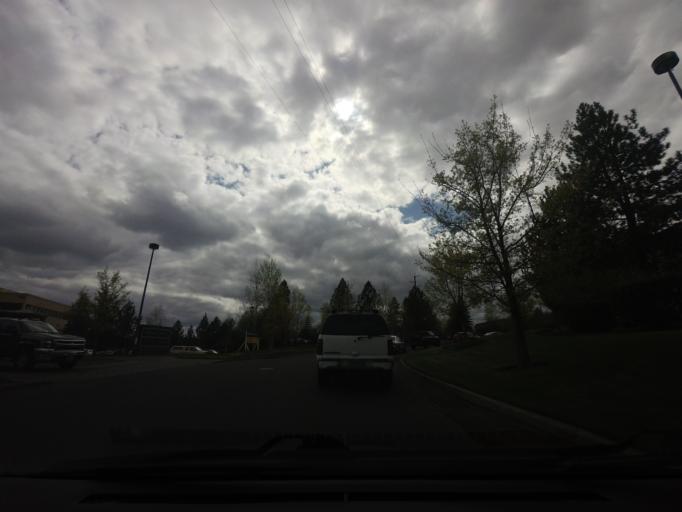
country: US
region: Oregon
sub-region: Deschutes County
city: Bend
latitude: 44.0434
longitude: -121.3244
